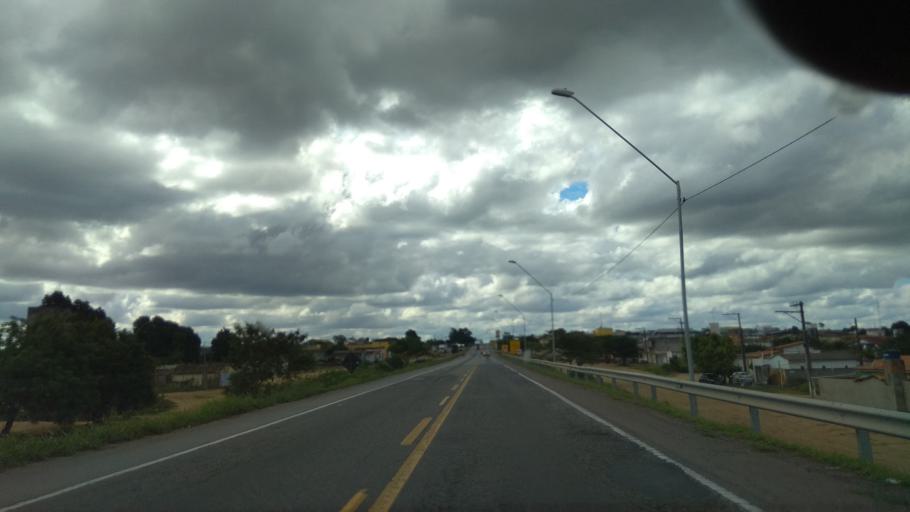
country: BR
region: Bahia
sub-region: Santa Ines
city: Santa Ines
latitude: -13.0785
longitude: -39.9618
